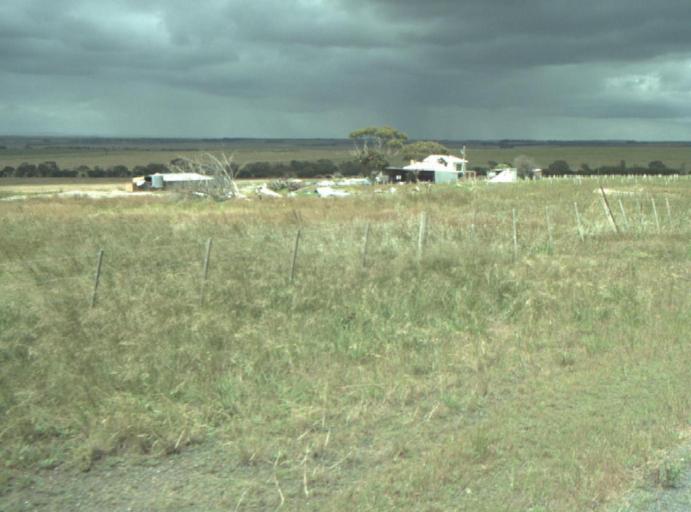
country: AU
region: Victoria
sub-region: Greater Geelong
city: Lara
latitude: -37.8922
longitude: 144.3736
